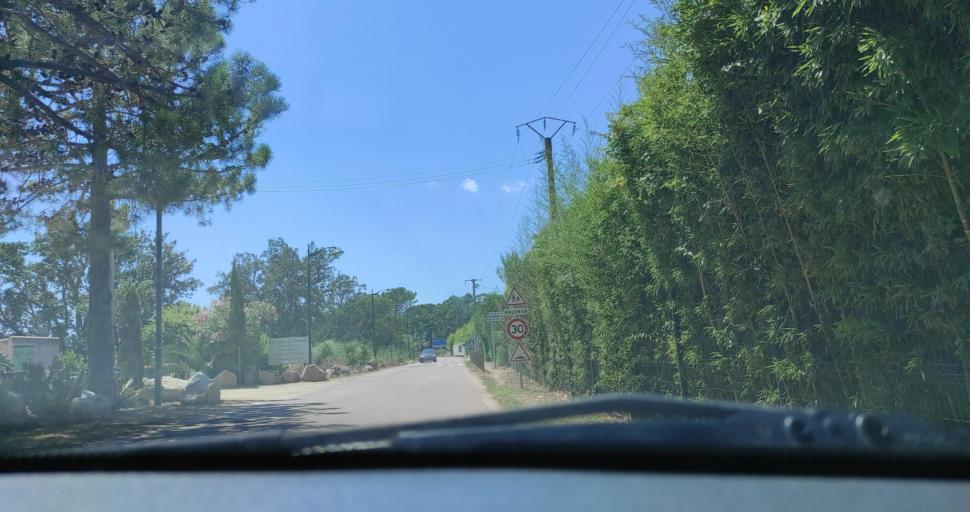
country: FR
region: Corsica
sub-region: Departement de la Corse-du-Sud
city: Porto-Vecchio
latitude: 41.6251
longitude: 9.3368
